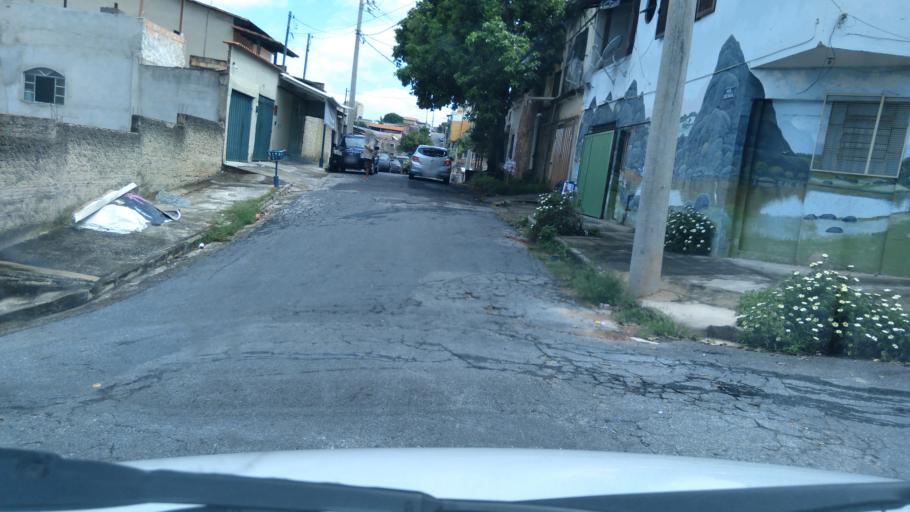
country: BR
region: Minas Gerais
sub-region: Belo Horizonte
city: Belo Horizonte
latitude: -19.8937
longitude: -43.8915
